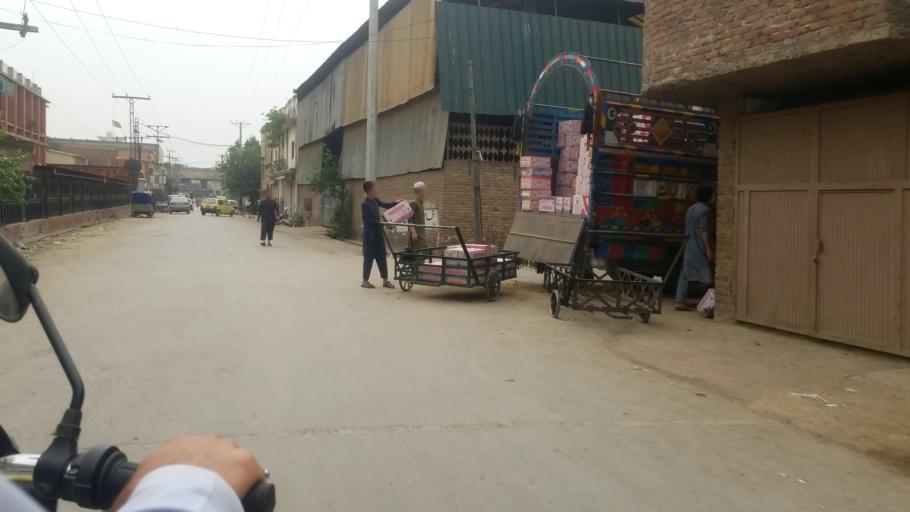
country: PK
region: Khyber Pakhtunkhwa
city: Peshawar
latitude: 33.9836
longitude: 71.5601
